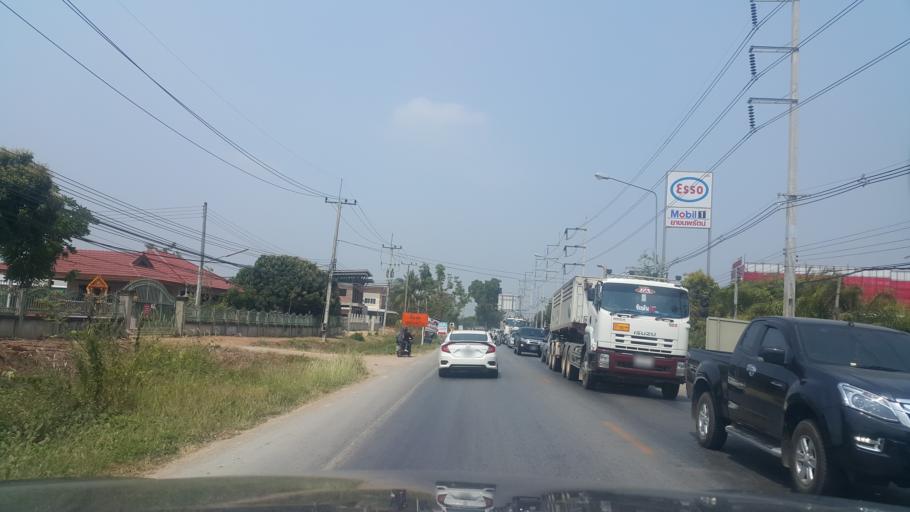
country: TH
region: Lamphun
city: Pa Sang
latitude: 18.4726
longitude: 98.9530
